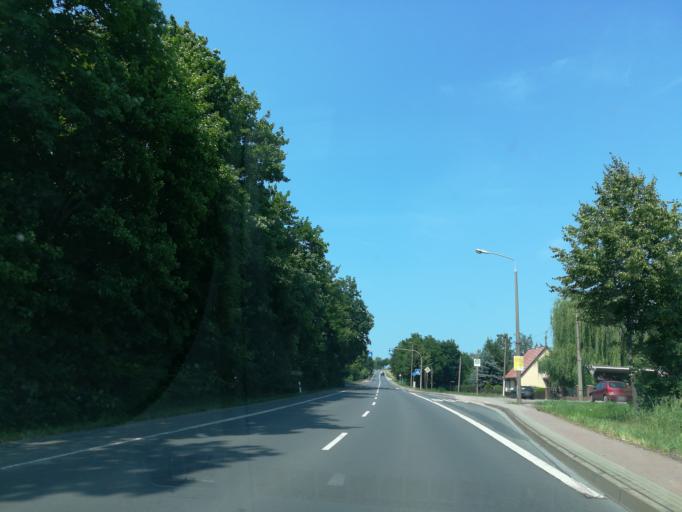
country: DE
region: Saxony-Anhalt
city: Aschersleben
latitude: 51.7739
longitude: 11.4564
